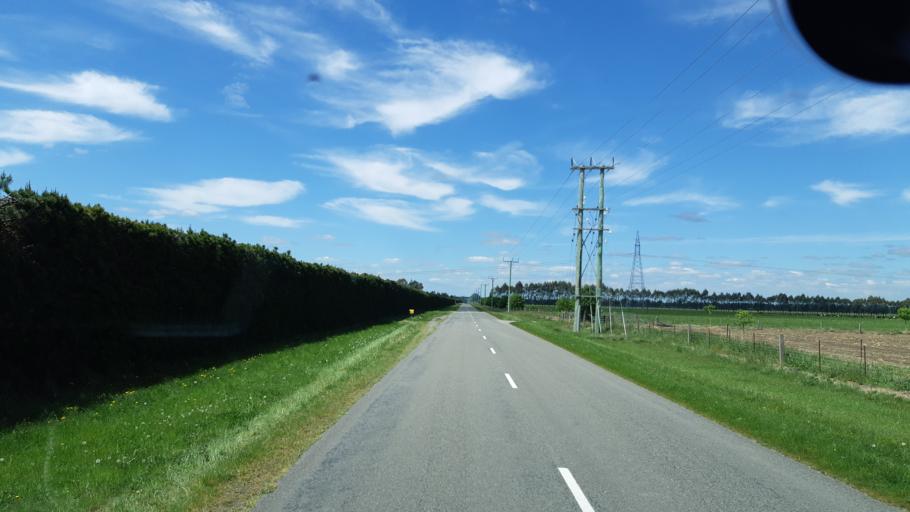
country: NZ
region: Canterbury
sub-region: Ashburton District
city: Methven
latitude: -43.7236
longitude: 171.4827
